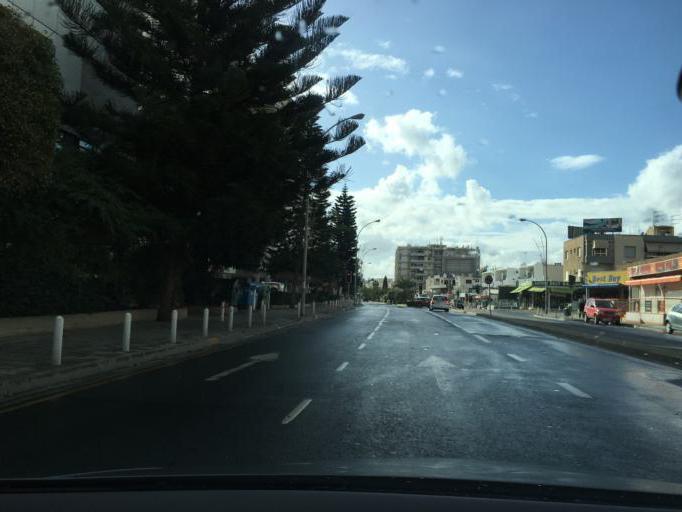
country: CY
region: Limassol
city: Mouttagiaka
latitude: 34.6992
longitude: 33.0985
